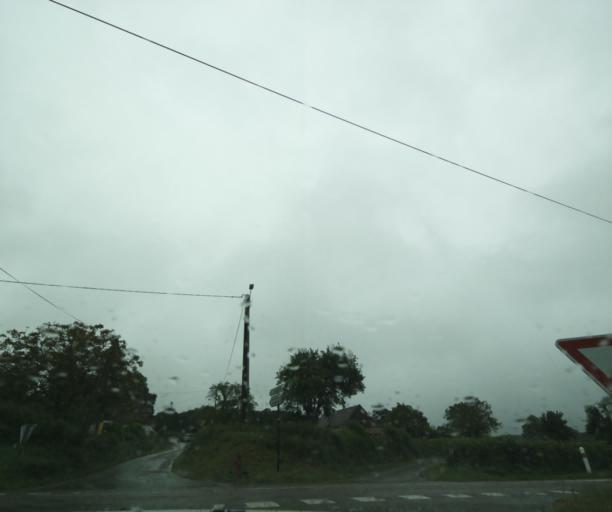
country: FR
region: Bourgogne
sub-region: Departement de Saone-et-Loire
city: Charolles
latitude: 46.3984
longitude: 4.2525
